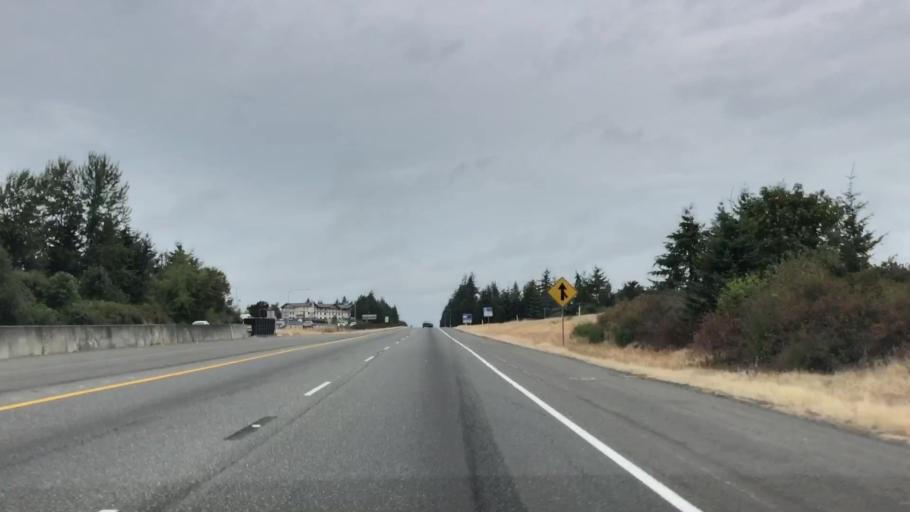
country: US
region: Washington
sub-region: Pierce County
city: Gig Harbor
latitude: 47.3059
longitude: -122.5768
